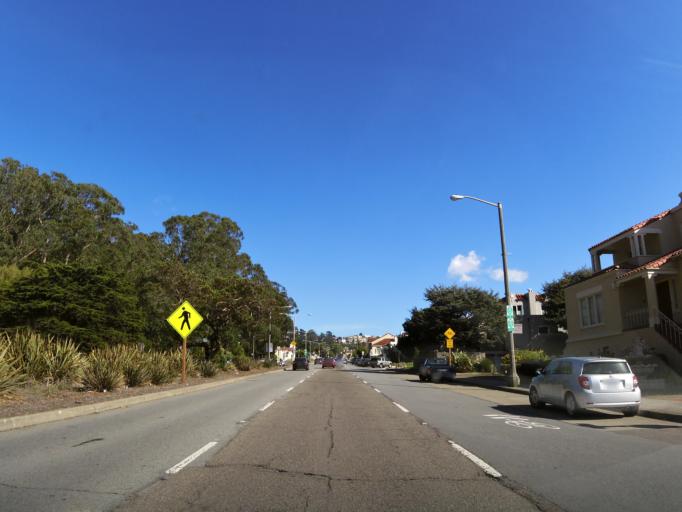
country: US
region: California
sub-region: San Mateo County
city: Daly City
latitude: 37.7345
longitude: -122.4781
